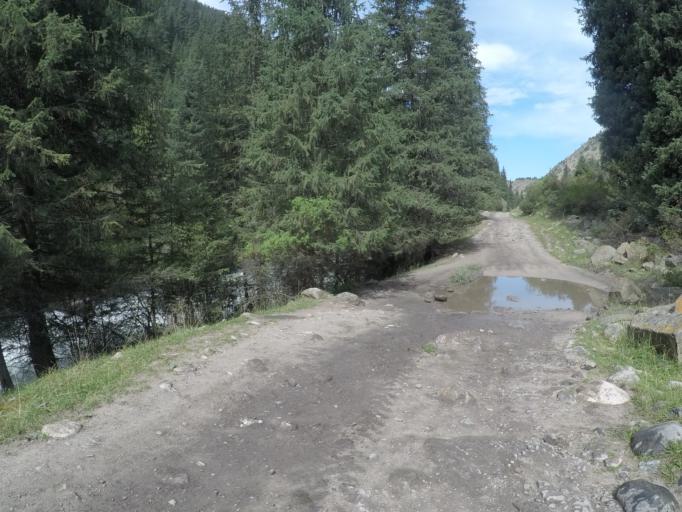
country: KG
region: Ysyk-Koel
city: Teploklyuchenka
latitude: 42.4366
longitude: 78.5615
